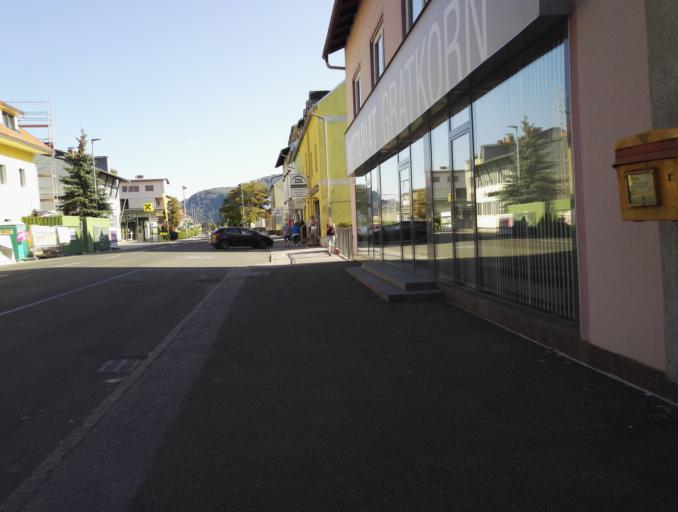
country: AT
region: Styria
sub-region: Politischer Bezirk Graz-Umgebung
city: Gratkorn
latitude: 47.1323
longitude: 15.3393
